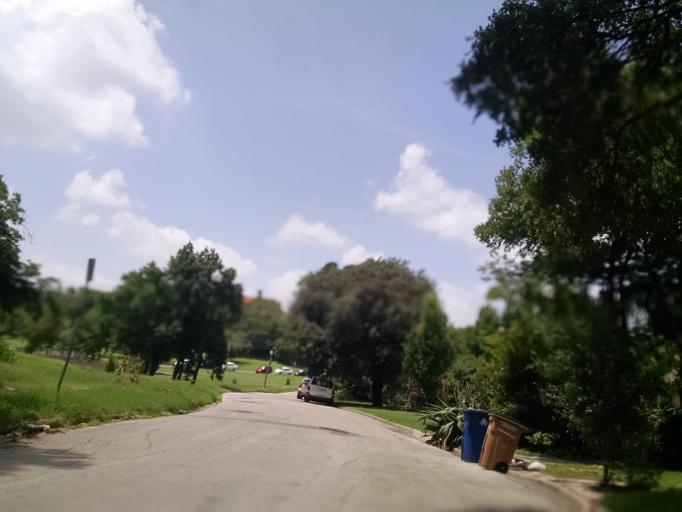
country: US
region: Texas
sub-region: Travis County
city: Austin
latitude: 30.2967
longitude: -97.7396
